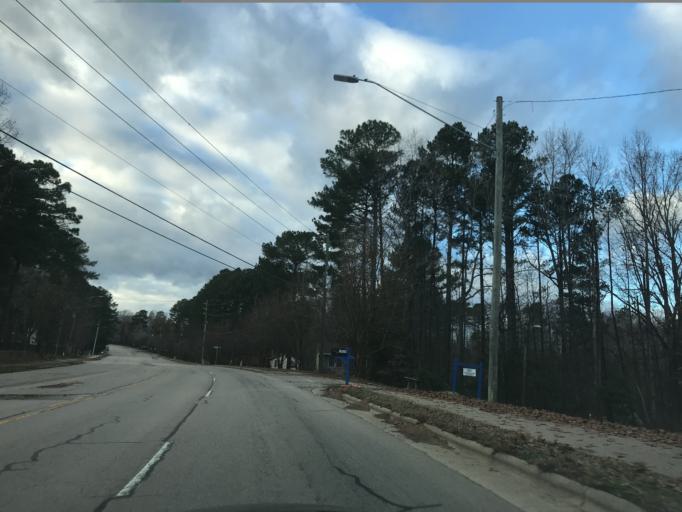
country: US
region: North Carolina
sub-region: Wake County
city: West Raleigh
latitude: 35.8704
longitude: -78.6549
